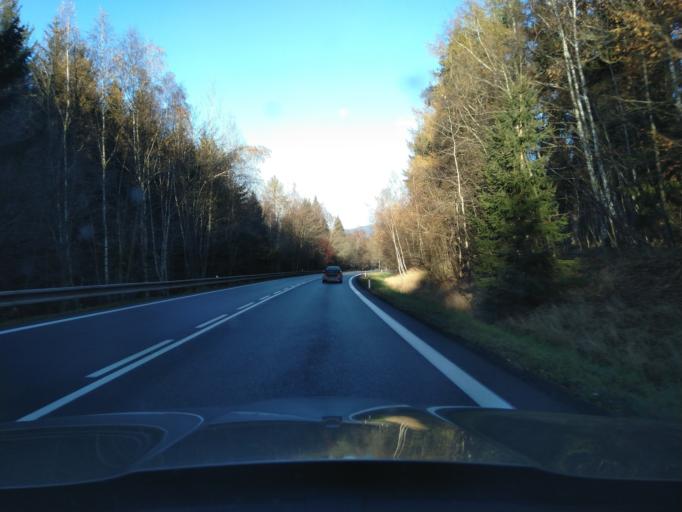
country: CZ
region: Jihocesky
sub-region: Okres Prachatice
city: Zdikov
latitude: 49.0753
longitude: 13.7064
